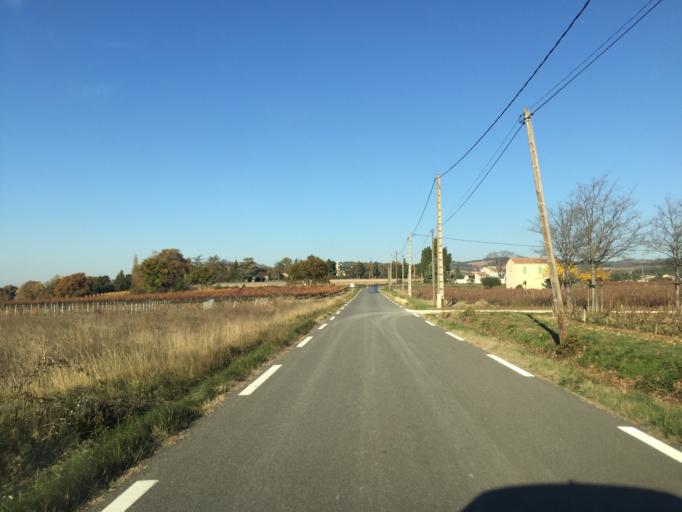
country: FR
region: Provence-Alpes-Cote d'Azur
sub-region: Departement du Vaucluse
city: Sainte-Cecile-les-Vignes
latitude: 44.2201
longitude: 4.9289
